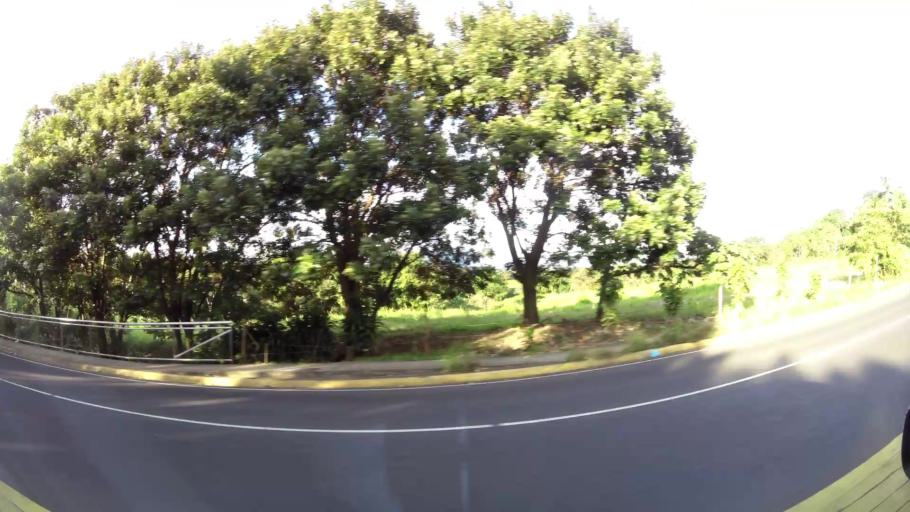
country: CR
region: Heredia
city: Llorente
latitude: 10.0048
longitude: -84.1733
